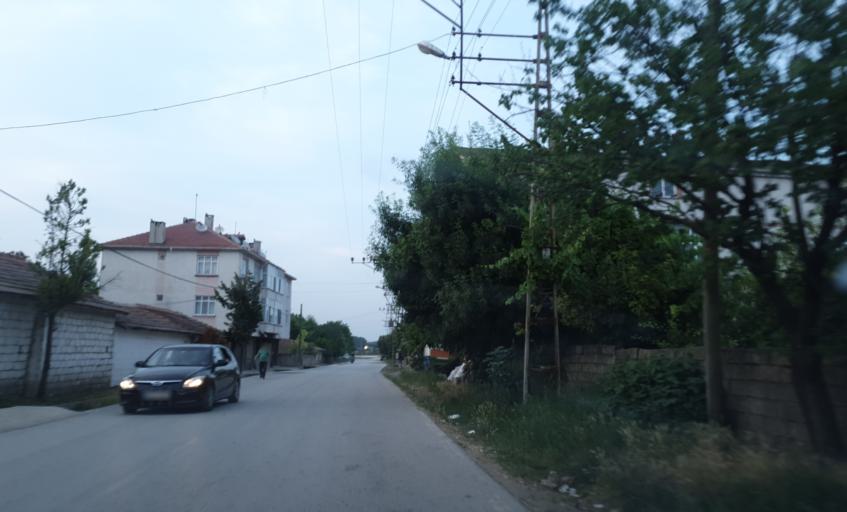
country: TR
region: Tekirdag
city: Beyazkoy
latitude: 41.3859
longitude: 27.6211
